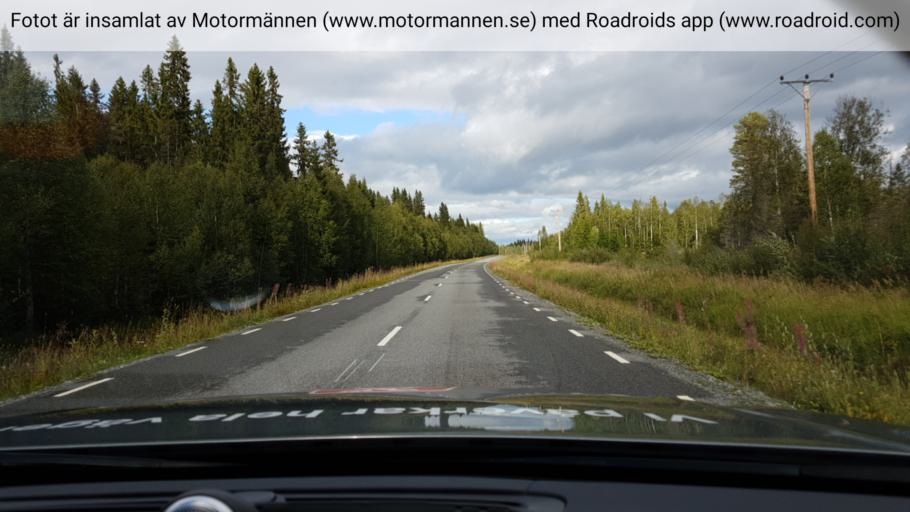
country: SE
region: Jaemtland
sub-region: Krokoms Kommun
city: Krokom
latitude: 63.6477
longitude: 14.4498
